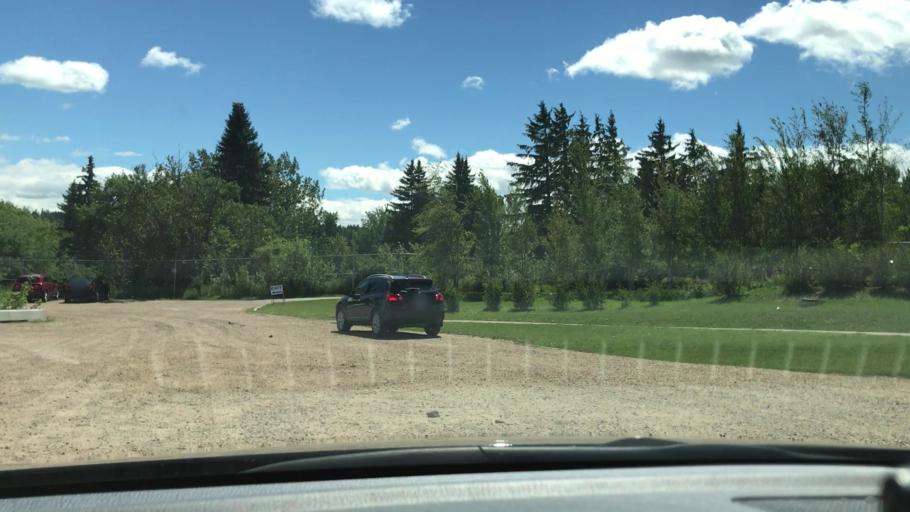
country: CA
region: Alberta
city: Edmonton
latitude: 53.5110
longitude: -113.5525
